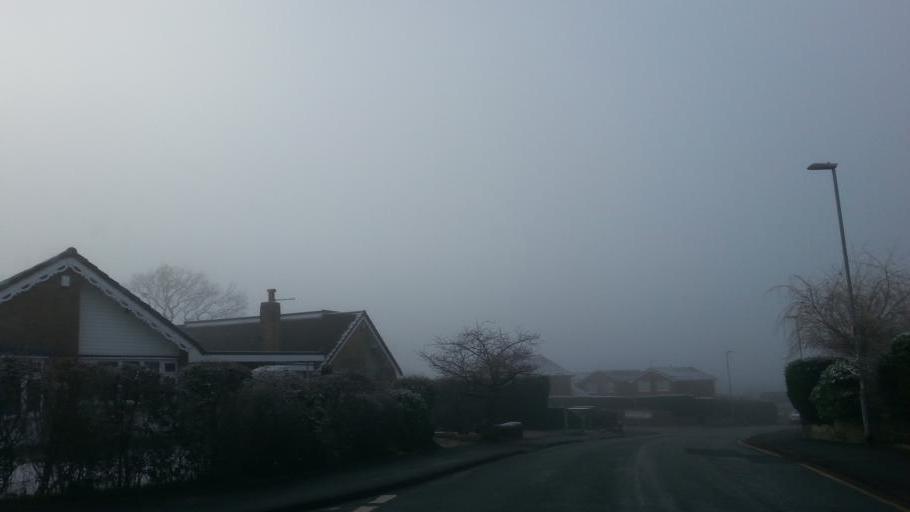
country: GB
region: England
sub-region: Staffordshire
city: Biddulph
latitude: 53.1213
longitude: -2.1586
